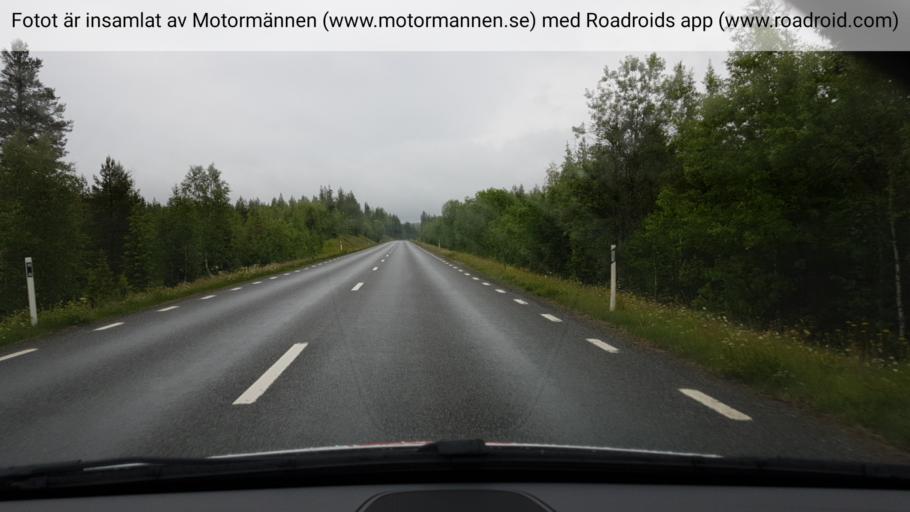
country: SE
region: Jaemtland
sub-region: OEstersunds Kommun
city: Lit
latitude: 63.4004
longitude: 15.0524
